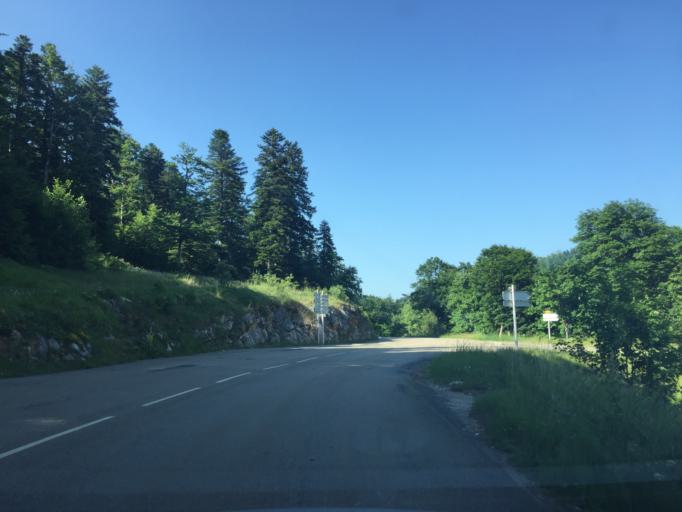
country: FR
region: Rhone-Alpes
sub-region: Departement de la Drome
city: Saint-Laurent-en-Royans
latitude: 44.9647
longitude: 5.3338
